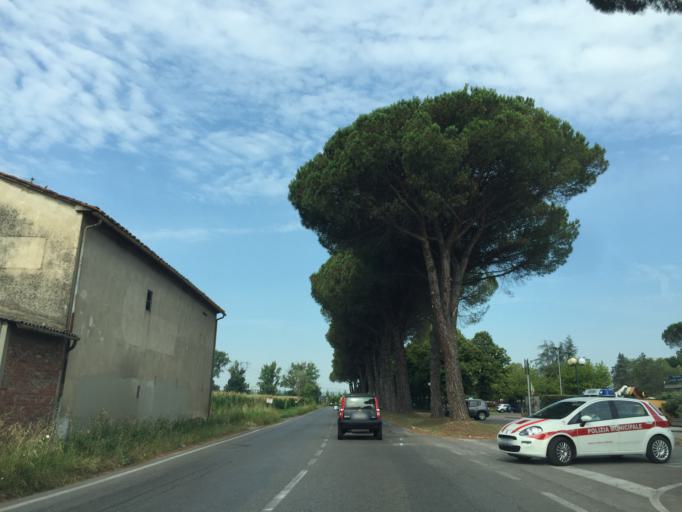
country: IT
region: Tuscany
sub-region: Provincia di Pistoia
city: Montecatini-Terme
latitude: 43.8575
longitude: 10.7706
